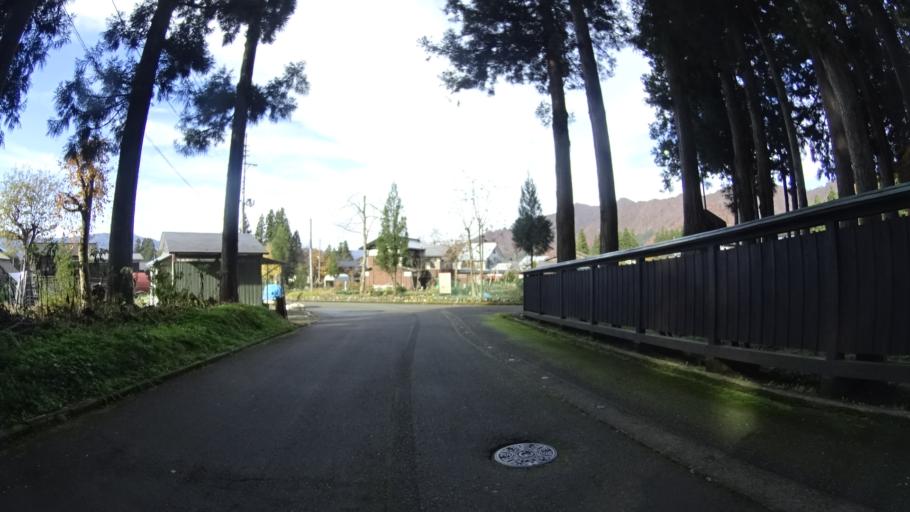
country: JP
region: Niigata
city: Muikamachi
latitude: 37.0316
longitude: 138.8892
